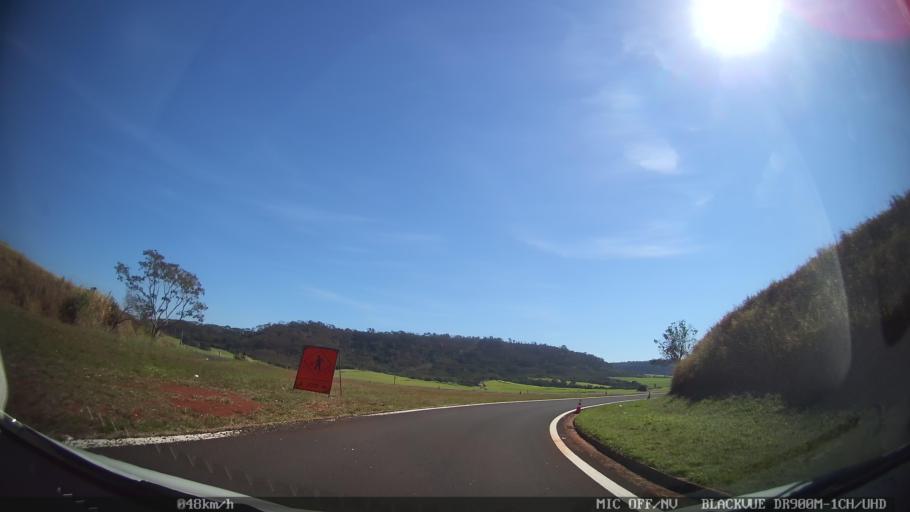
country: BR
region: Sao Paulo
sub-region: Sao Simao
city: Sao Simao
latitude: -21.5291
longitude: -47.6435
